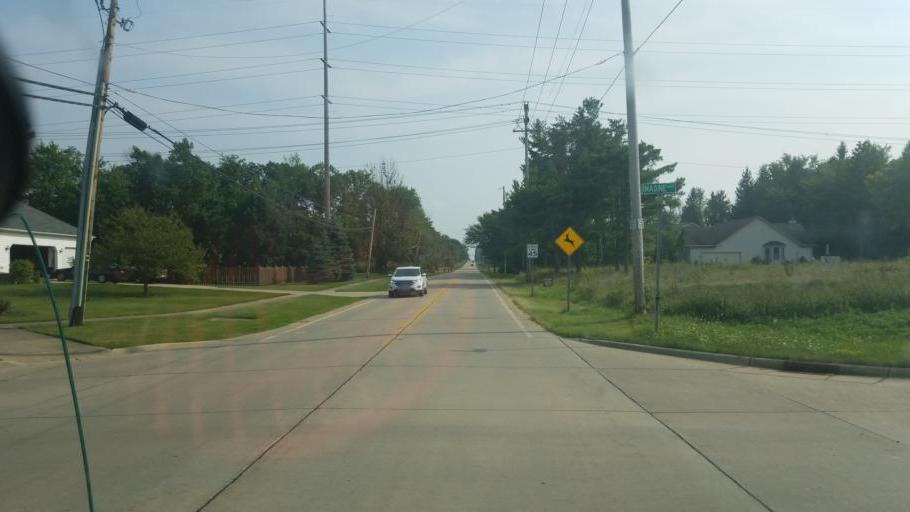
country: US
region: Ohio
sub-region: Medina County
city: Medina
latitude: 41.1205
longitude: -81.8840
